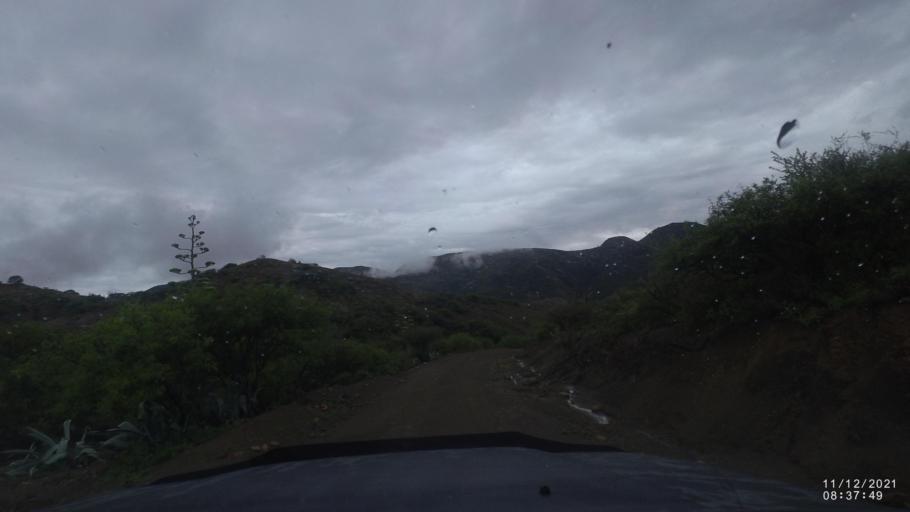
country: BO
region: Cochabamba
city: Tarata
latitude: -17.9249
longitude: -65.9370
